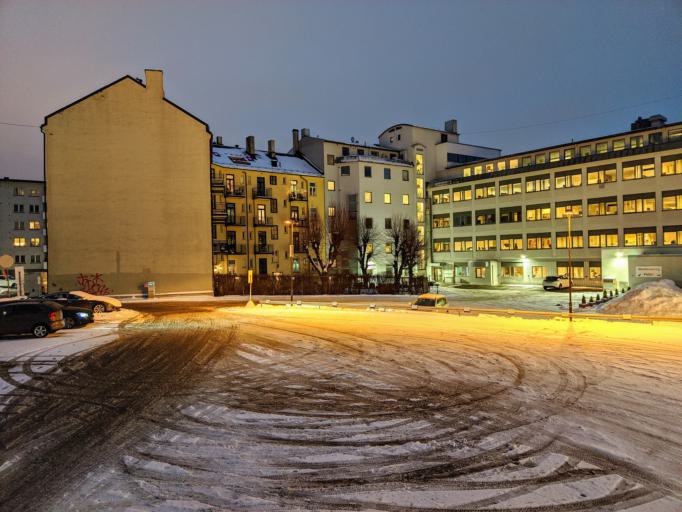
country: NO
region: Oslo
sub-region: Oslo
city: Oslo
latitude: 59.9423
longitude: 10.7691
